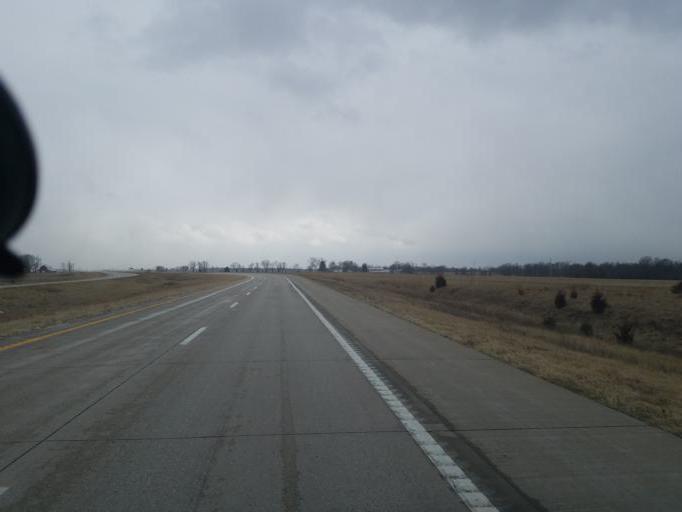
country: US
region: Missouri
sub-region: Randolph County
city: Huntsville
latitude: 39.5753
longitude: -92.4658
